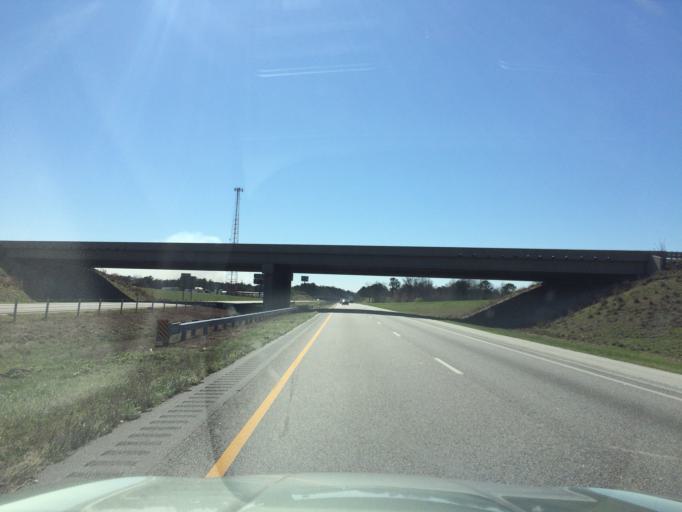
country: US
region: Alabama
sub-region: Lee County
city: Auburn
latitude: 32.5485
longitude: -85.5270
